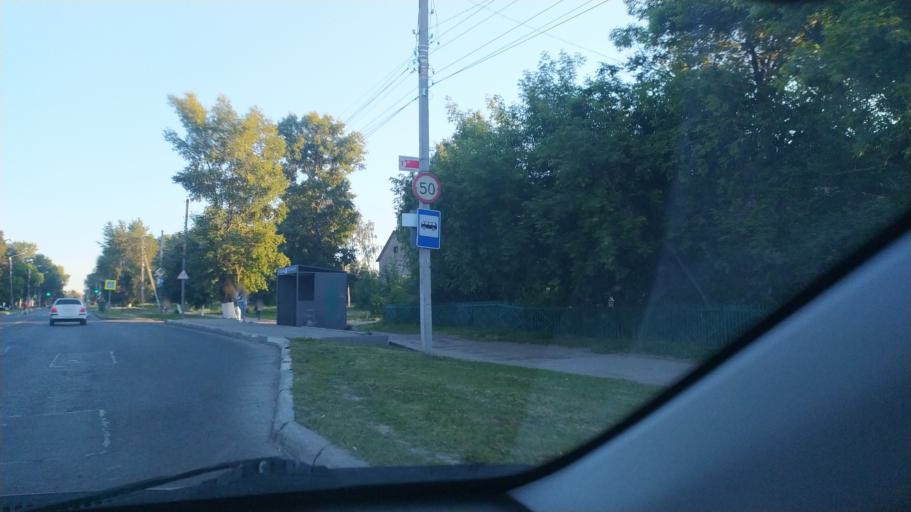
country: RU
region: Chuvashia
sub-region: Cheboksarskiy Rayon
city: Cheboksary
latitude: 56.1228
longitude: 47.2274
